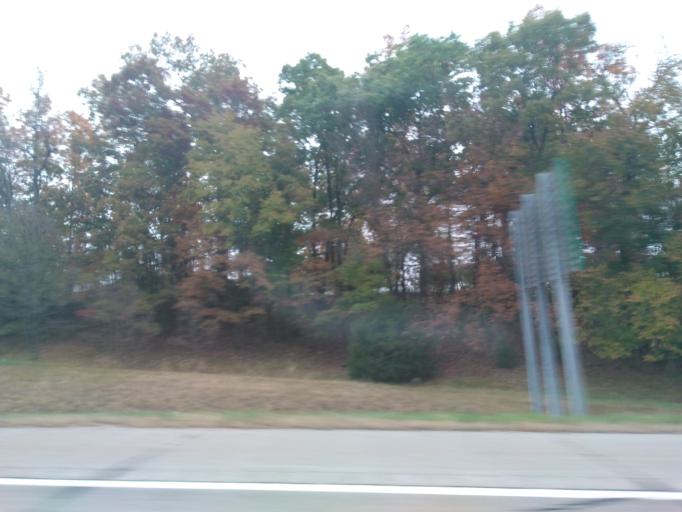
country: US
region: Missouri
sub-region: Saint Louis County
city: Oakville
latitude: 38.4913
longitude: -90.2913
